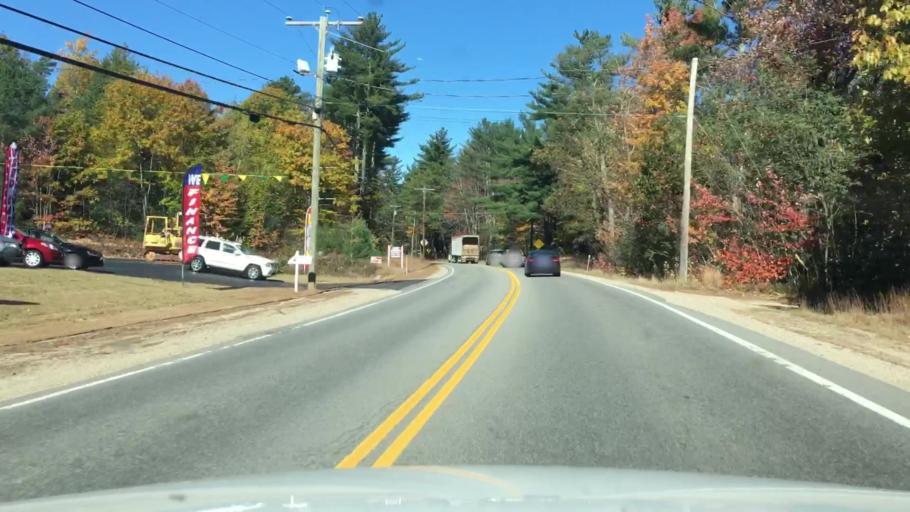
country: US
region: New Hampshire
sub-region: Carroll County
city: Ossipee
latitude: 43.7067
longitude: -71.1130
